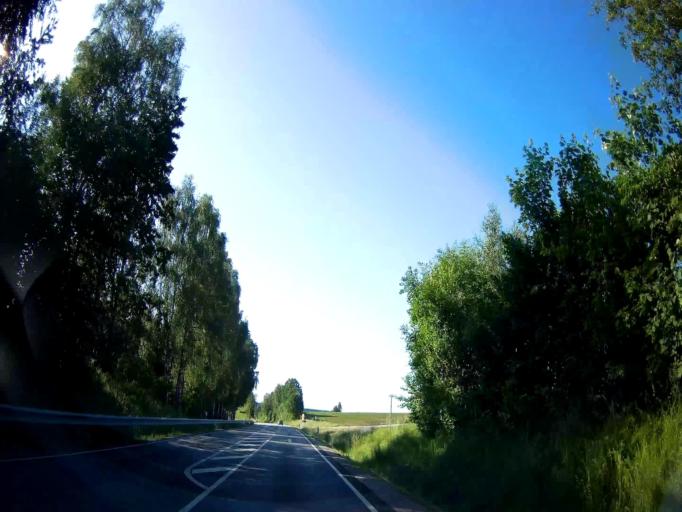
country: DE
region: Bavaria
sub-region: Lower Bavaria
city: Wurmannsquick
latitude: 48.3579
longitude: 12.7956
